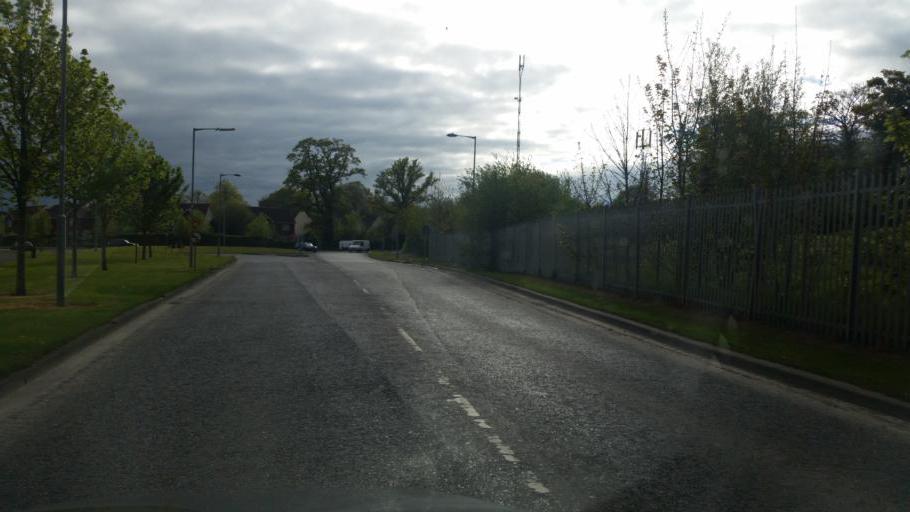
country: IE
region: Leinster
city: Hartstown
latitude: 53.3995
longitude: -6.4406
